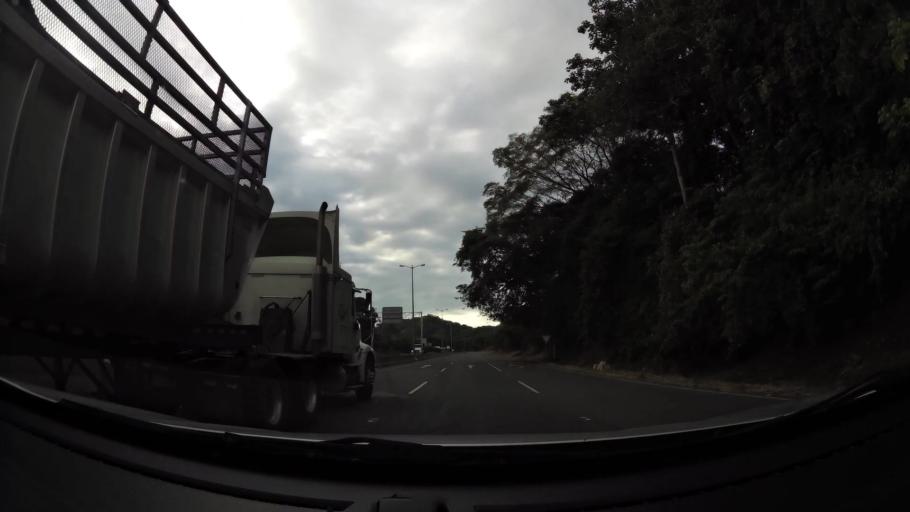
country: CR
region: Puntarenas
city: Esparza
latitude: 9.9141
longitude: -84.6777
